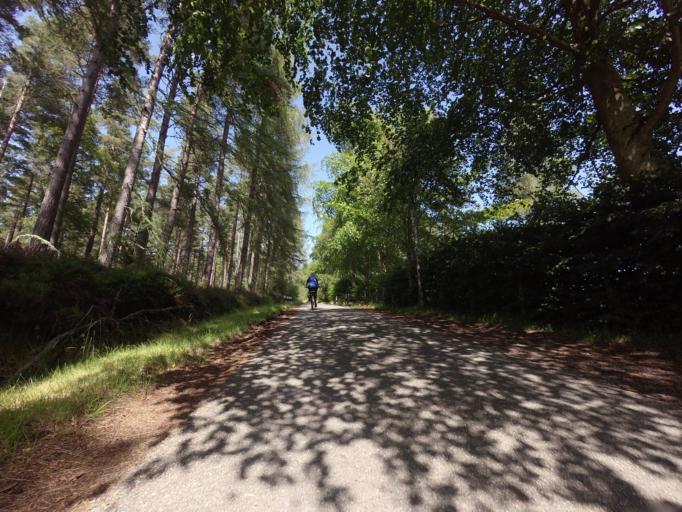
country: GB
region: Scotland
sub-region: Highland
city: Nairn
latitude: 57.4971
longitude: -3.9649
